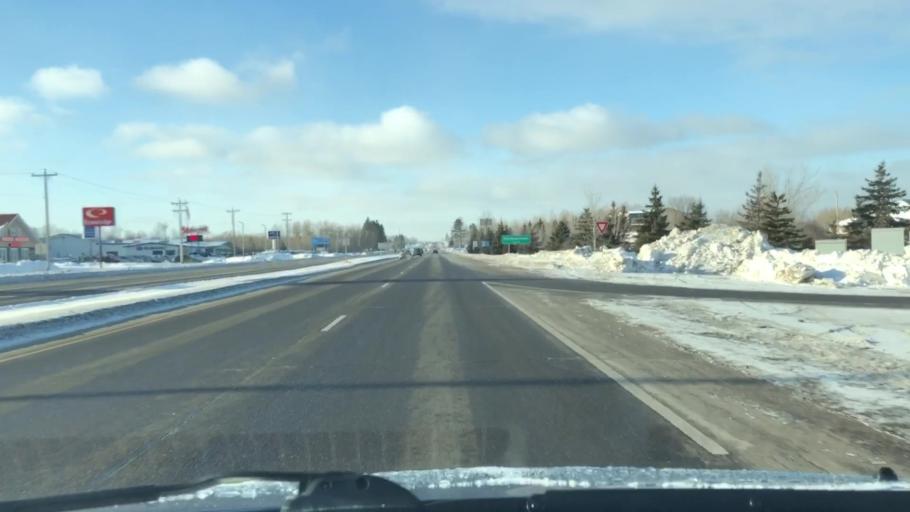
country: US
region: Minnesota
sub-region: Saint Louis County
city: Hermantown
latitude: 46.8151
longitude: -92.1750
